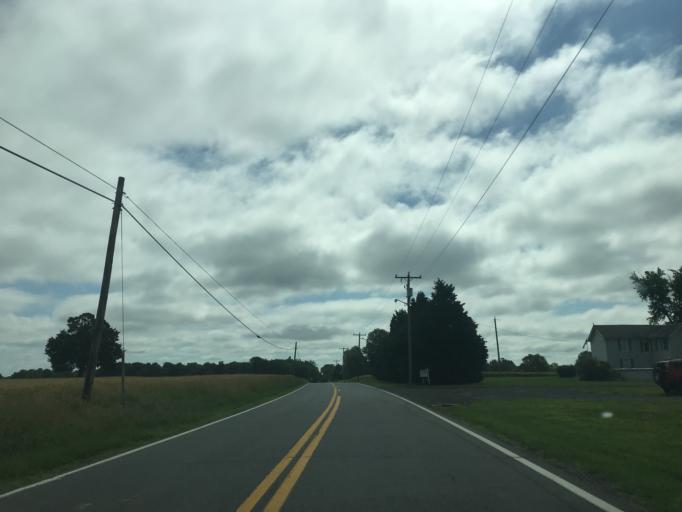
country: US
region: Maryland
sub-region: Caroline County
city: Ridgely
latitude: 38.8850
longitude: -75.9765
